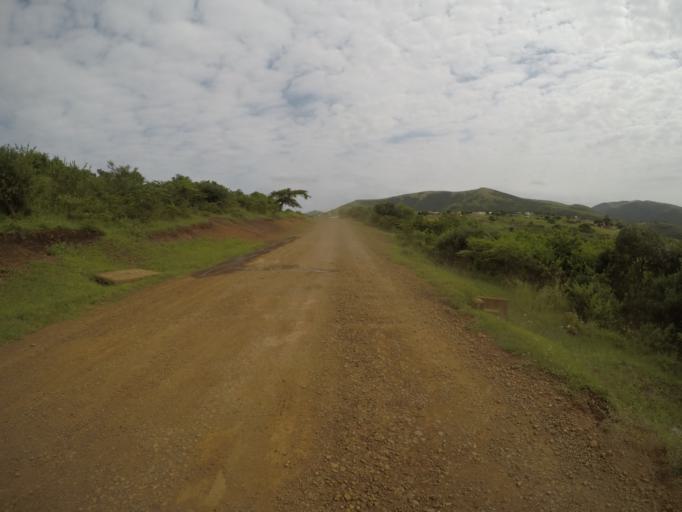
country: ZA
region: KwaZulu-Natal
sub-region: uThungulu District Municipality
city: Empangeni
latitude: -28.6227
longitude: 31.9061
